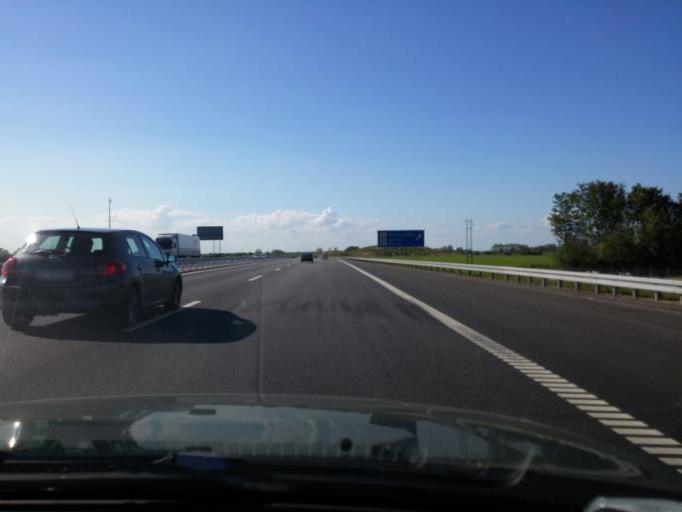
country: DK
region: South Denmark
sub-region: Middelfart Kommune
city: Norre Aby
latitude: 55.4706
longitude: 9.8955
